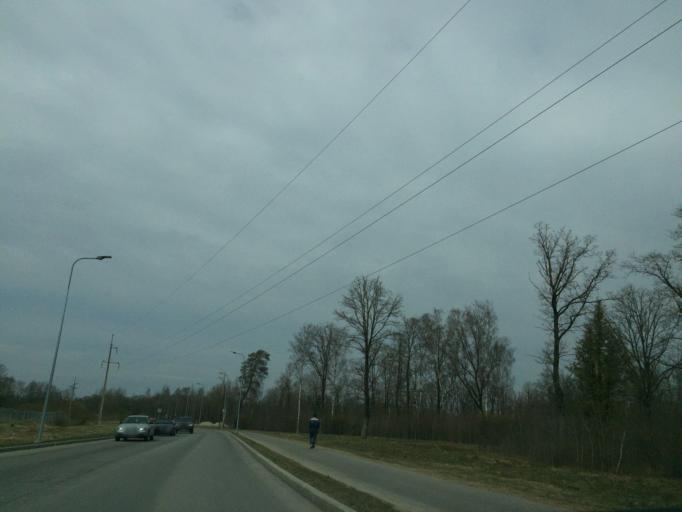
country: EE
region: Ida-Virumaa
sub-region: Narva linn
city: Narva
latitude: 59.3966
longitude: 28.1783
